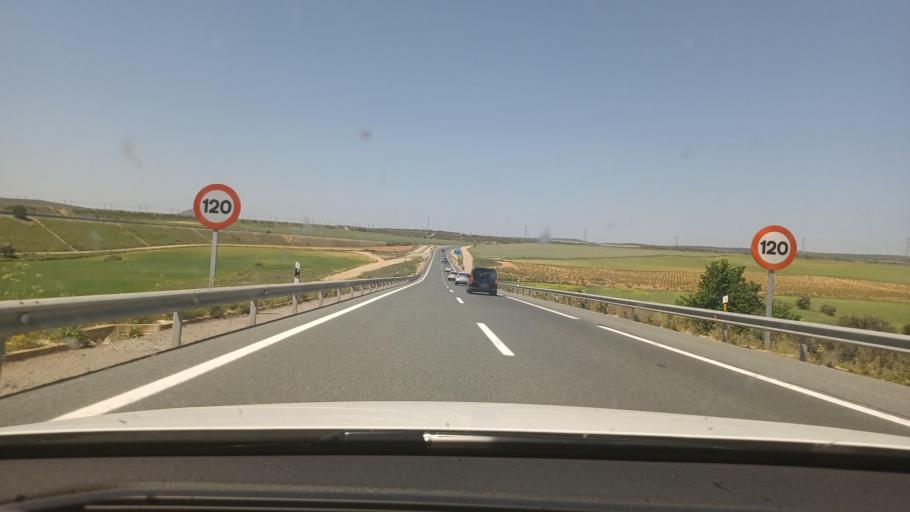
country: ES
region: Castille-La Mancha
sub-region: Provincia de Albacete
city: Alpera
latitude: 38.8785
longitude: -1.2282
